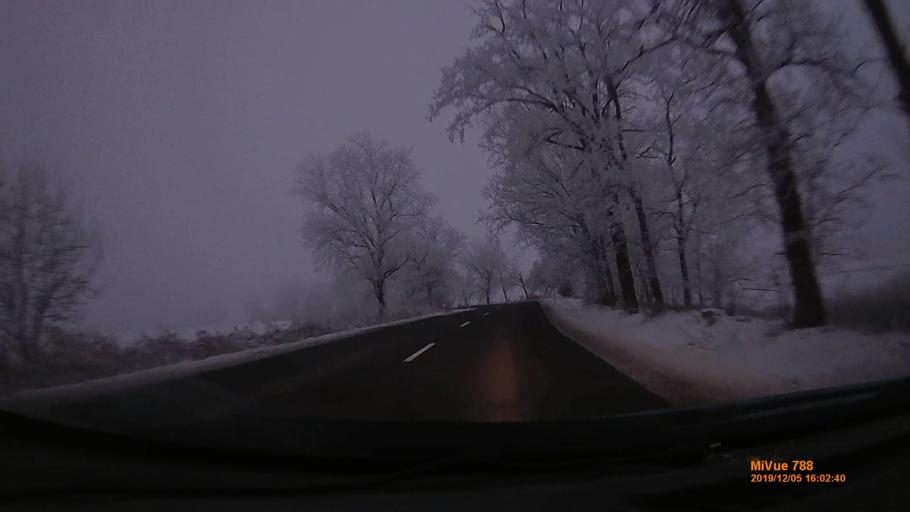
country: HU
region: Borsod-Abauj-Zemplen
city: Tokaj
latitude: 48.1008
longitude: 21.3794
